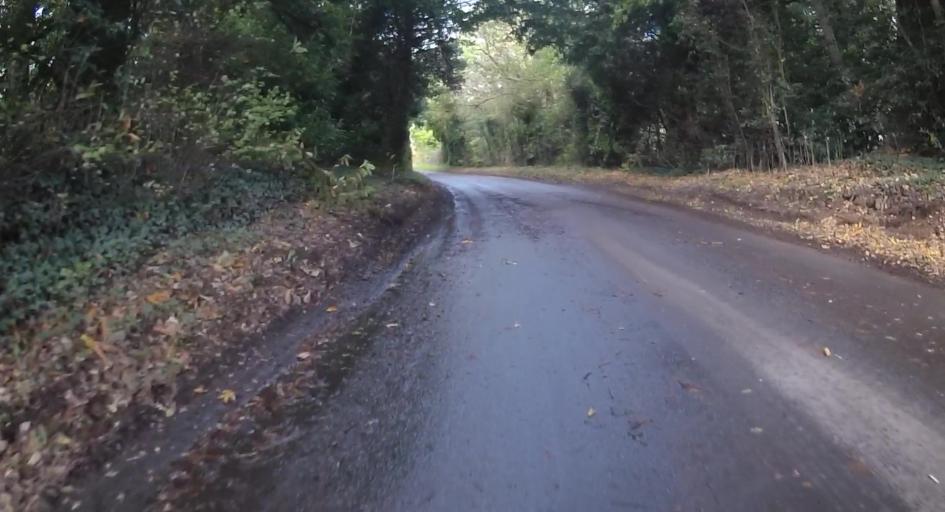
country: GB
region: England
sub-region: West Berkshire
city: Stratfield Mortimer
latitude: 51.3576
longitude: -1.0027
